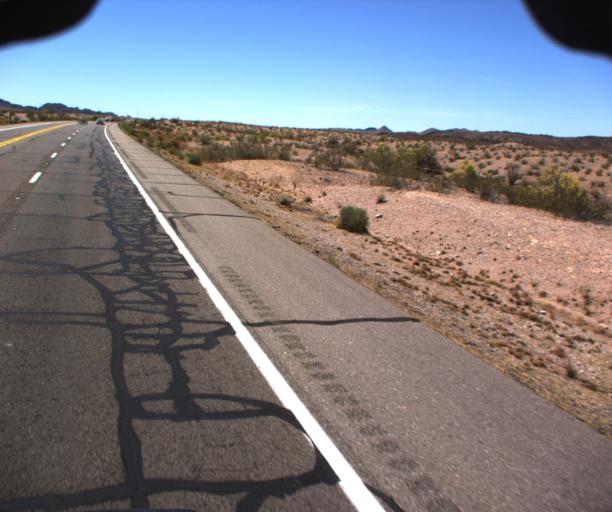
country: US
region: Arizona
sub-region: Mohave County
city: Desert Hills
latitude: 34.6897
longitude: -114.3024
